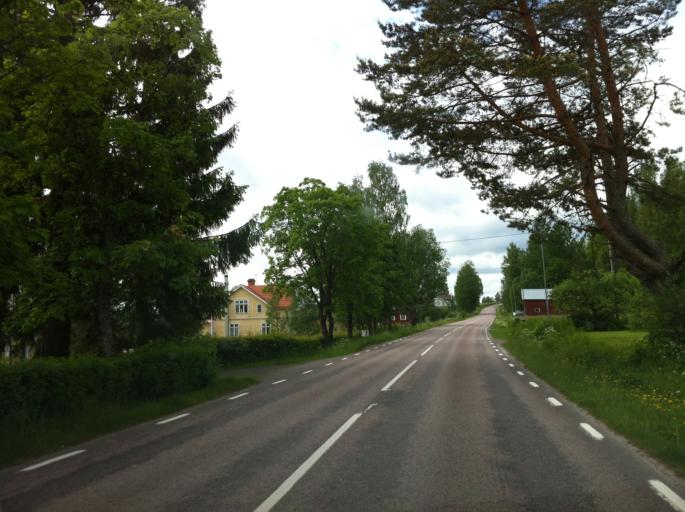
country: SE
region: Vaermland
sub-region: Sunne Kommun
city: Sunne
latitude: 59.8764
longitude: 13.1740
